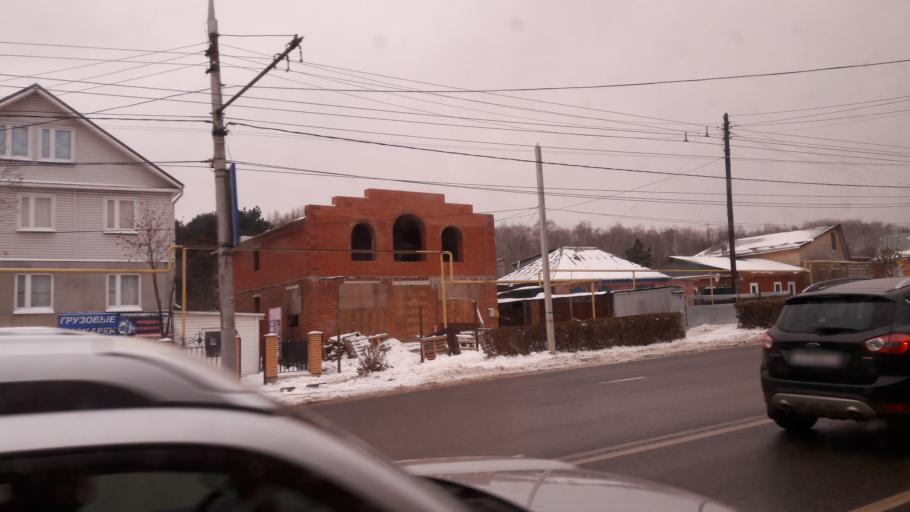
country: RU
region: Tula
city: Gorelki
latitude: 54.2330
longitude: 37.6246
